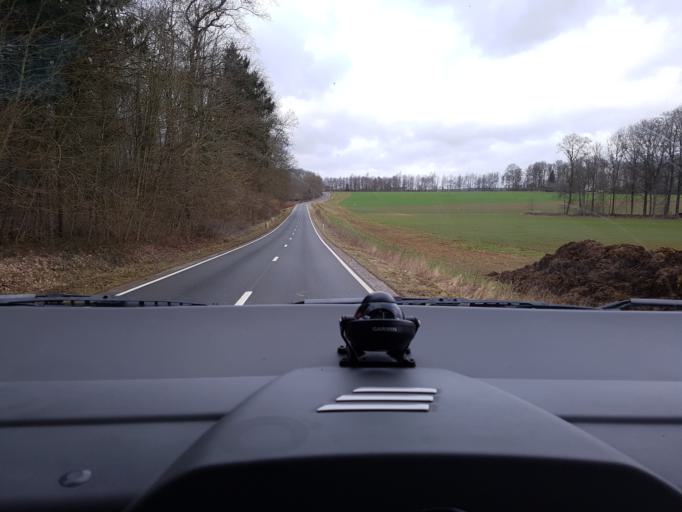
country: BE
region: Wallonia
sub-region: Province de Namur
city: Ciney
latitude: 50.2860
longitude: 5.1328
